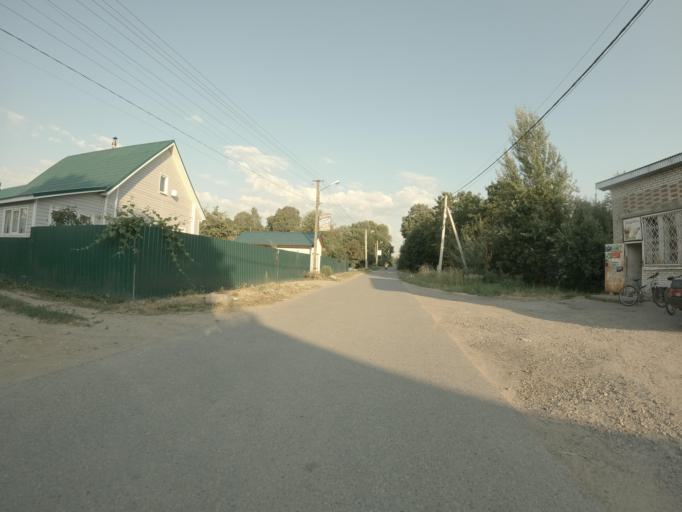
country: RU
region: Leningrad
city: Koltushi
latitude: 59.8885
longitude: 30.7107
